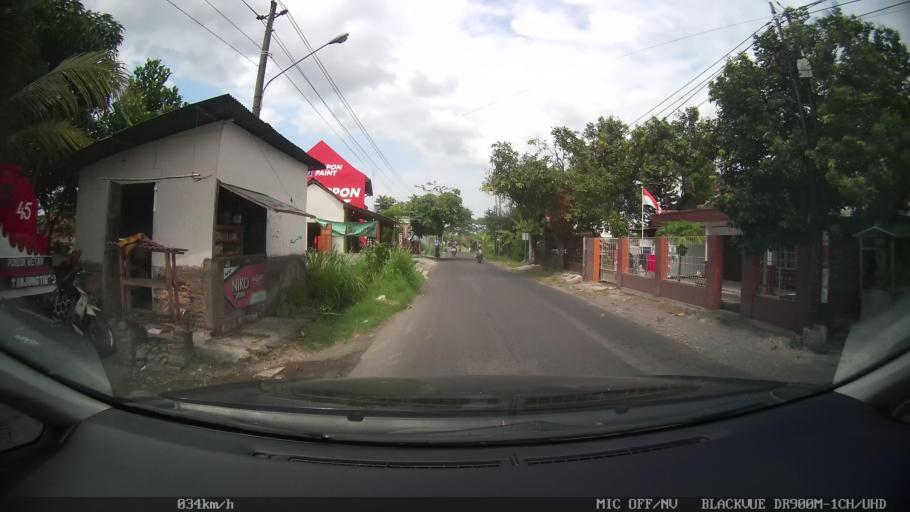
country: ID
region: Daerah Istimewa Yogyakarta
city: Depok
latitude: -7.7921
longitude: 110.4588
